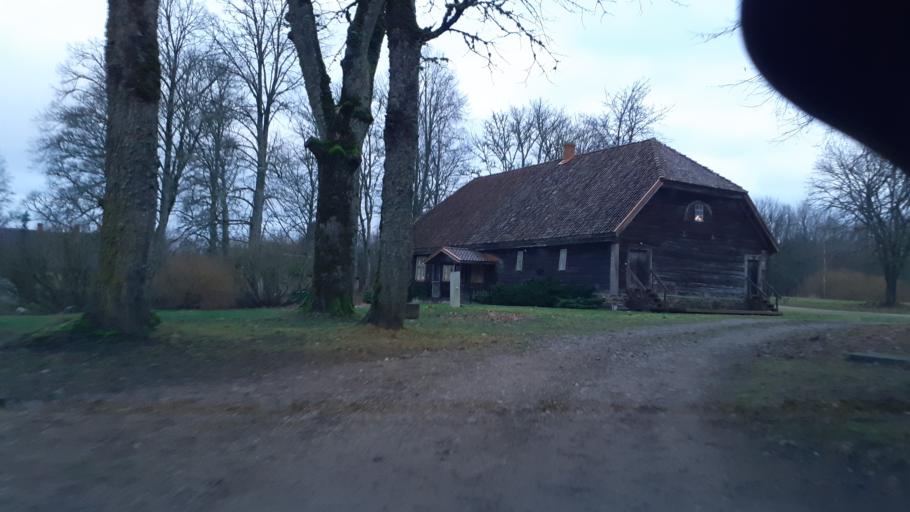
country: LV
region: Alsunga
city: Alsunga
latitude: 56.9046
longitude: 21.6959
